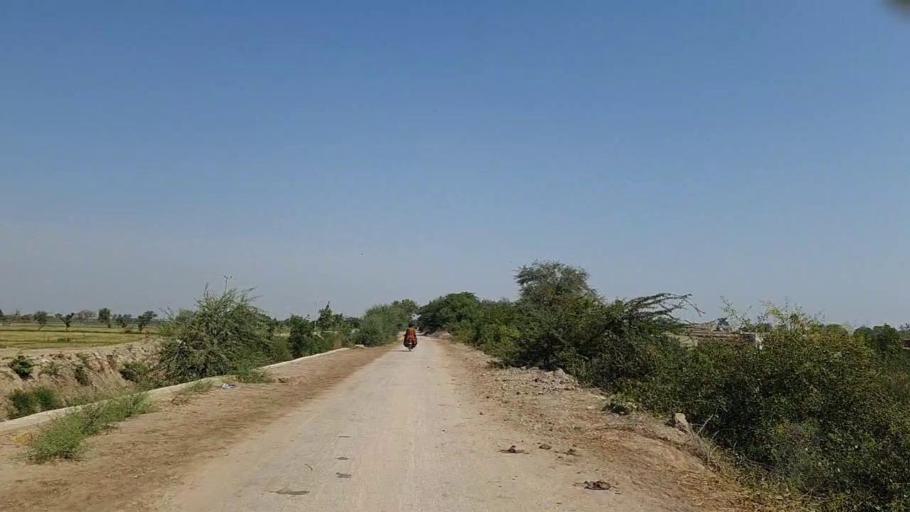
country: PK
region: Sindh
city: Mirpur Batoro
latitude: 24.6927
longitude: 68.2576
